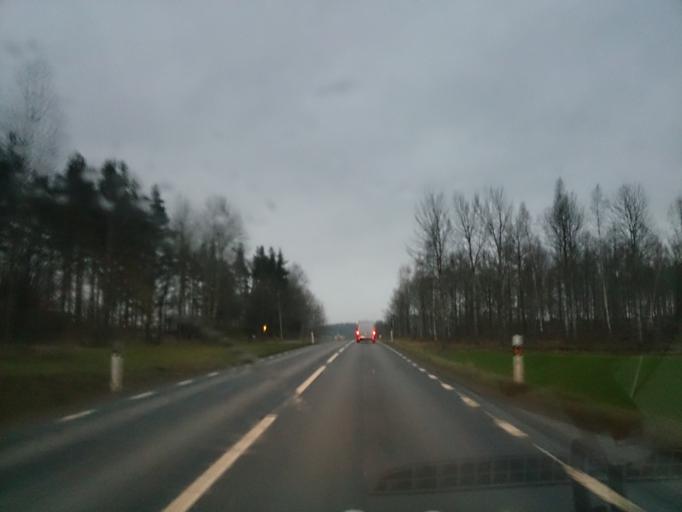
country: SE
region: OEstergoetland
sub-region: Linkopings Kommun
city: Linghem
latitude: 58.3799
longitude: 15.7976
